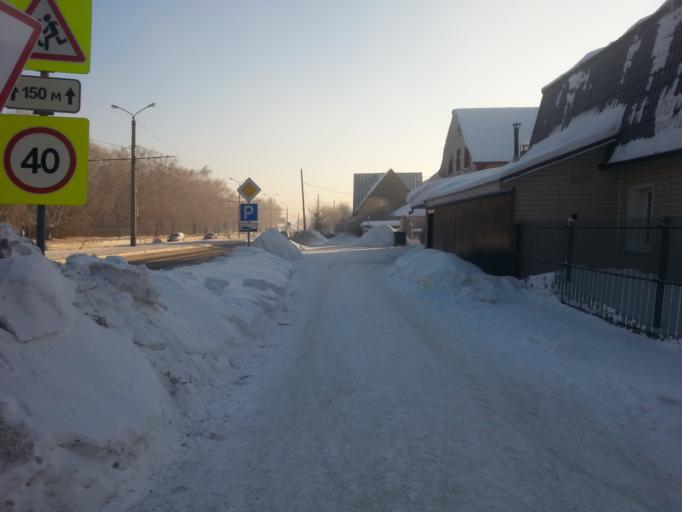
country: RU
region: Altai Krai
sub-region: Gorod Barnaulskiy
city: Barnaul
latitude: 53.3530
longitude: 83.7237
